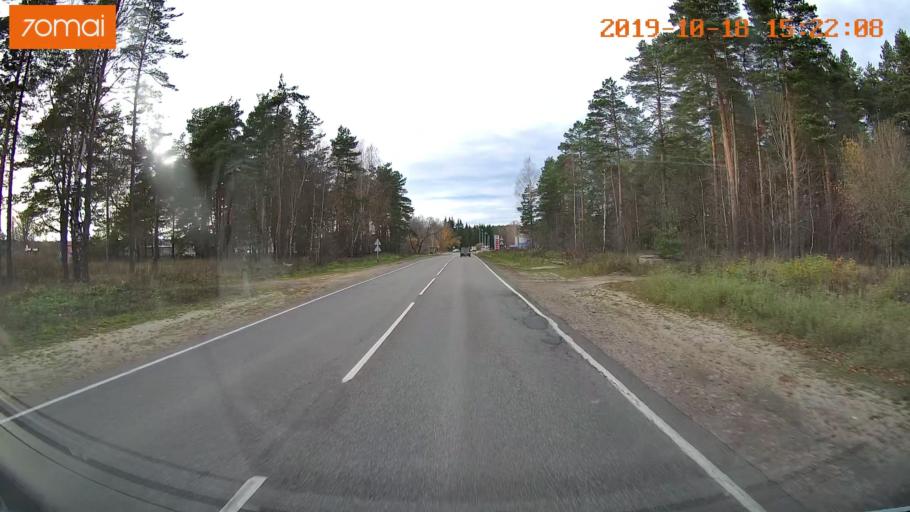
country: RU
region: Vladimir
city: Anopino
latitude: 55.7059
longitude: 40.7371
